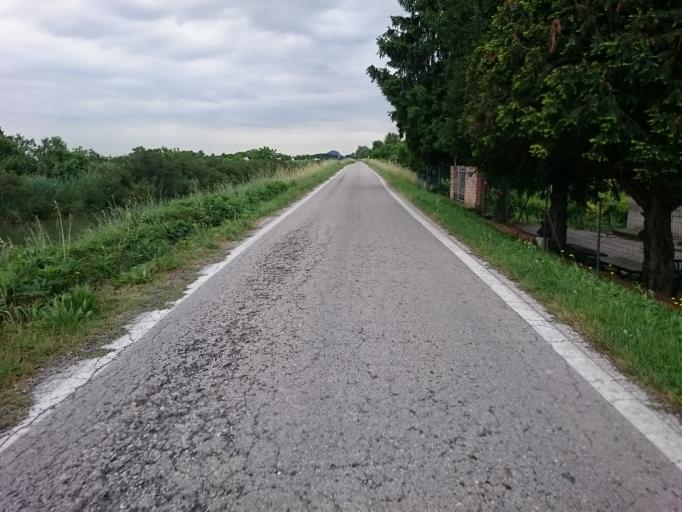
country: IT
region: Veneto
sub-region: Provincia di Padova
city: Montegrotto Terme
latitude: 45.3105
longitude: 11.7995
